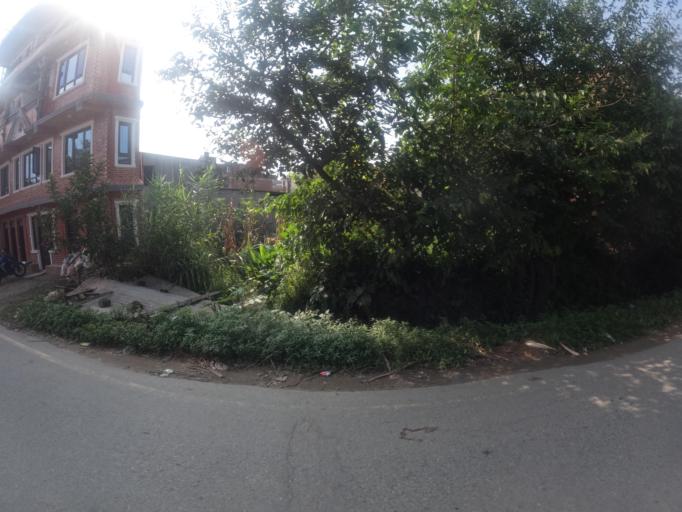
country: NP
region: Central Region
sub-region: Bagmati Zone
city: Bhaktapur
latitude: 27.6784
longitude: 85.4343
